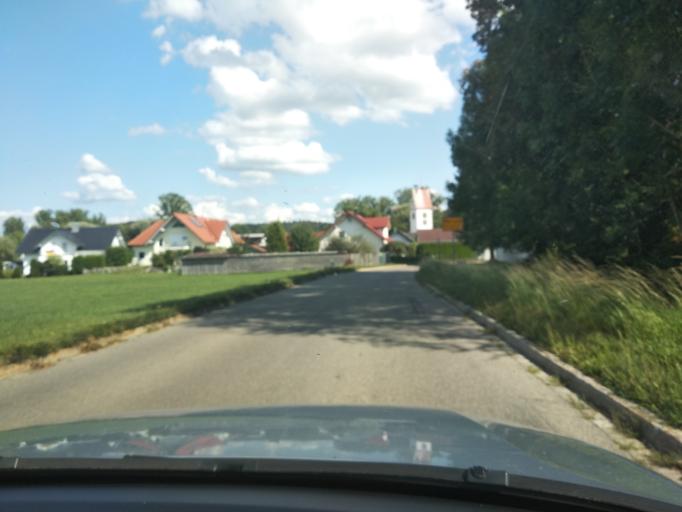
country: DE
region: Baden-Wuerttemberg
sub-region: Tuebingen Region
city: Leutkirch im Allgau
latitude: 47.8535
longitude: 10.0147
